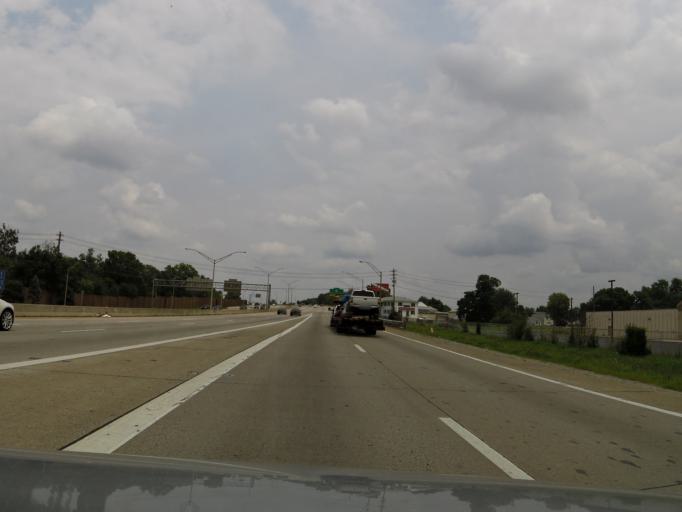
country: US
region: Kentucky
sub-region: Jefferson County
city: Audubon Park
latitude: 38.1906
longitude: -85.7207
